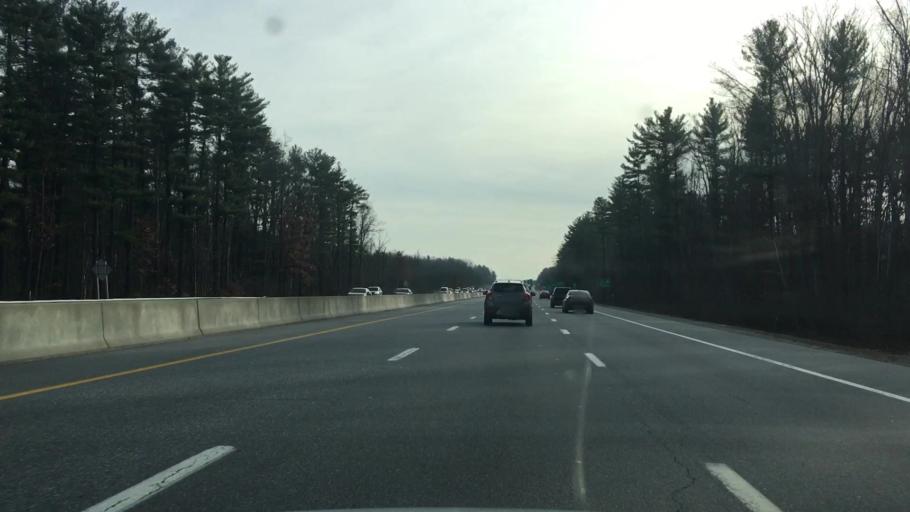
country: US
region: New Hampshire
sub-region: Hillsborough County
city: Bedford
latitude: 42.9364
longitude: -71.4691
